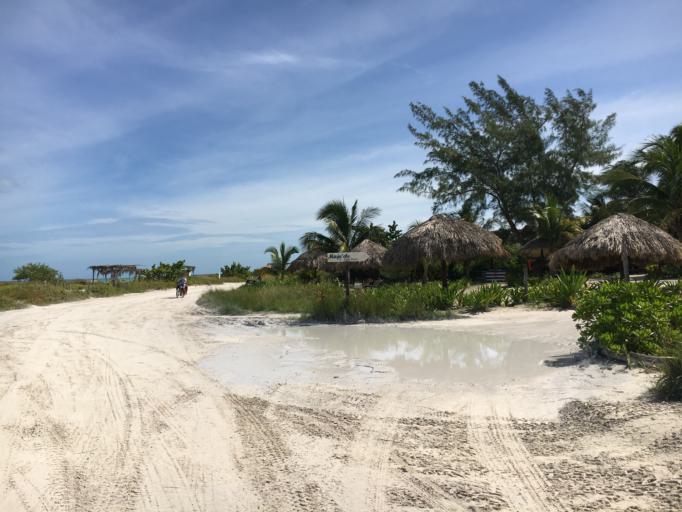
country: MX
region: Quintana Roo
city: Kantunilkin
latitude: 21.5274
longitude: -87.3754
